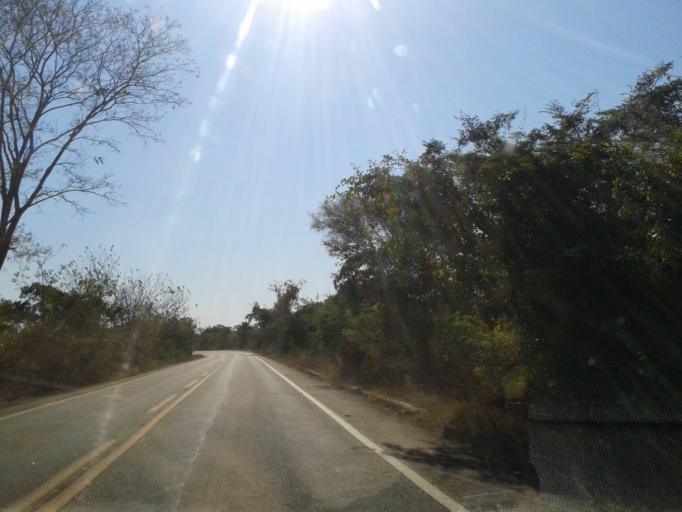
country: BR
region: Goias
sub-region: Mozarlandia
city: Mozarlandia
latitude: -14.6527
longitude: -50.5227
